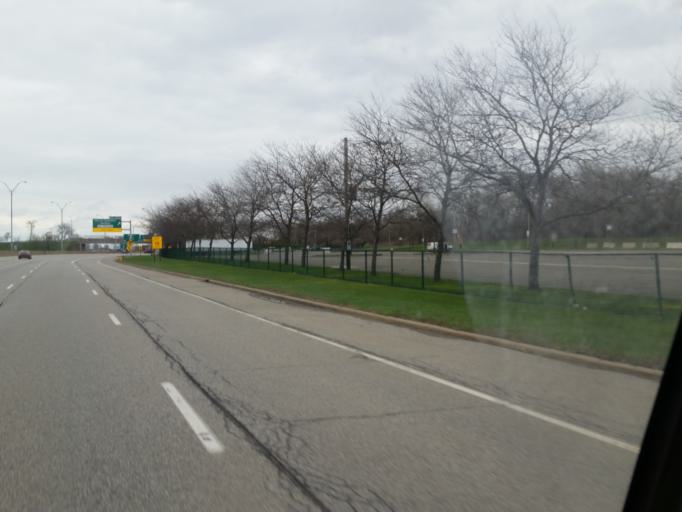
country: US
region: Ohio
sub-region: Cuyahoga County
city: Cleveland
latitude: 41.5128
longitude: -81.6838
